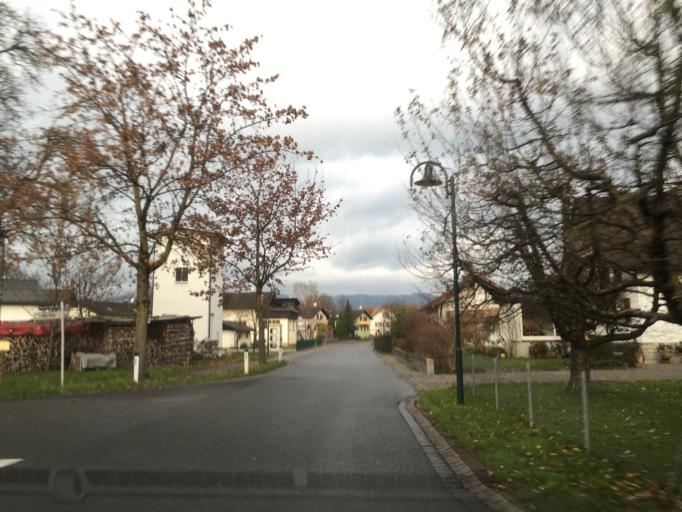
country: AT
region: Vorarlberg
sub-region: Politischer Bezirk Feldkirch
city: Mader
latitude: 47.3437
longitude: 9.6237
